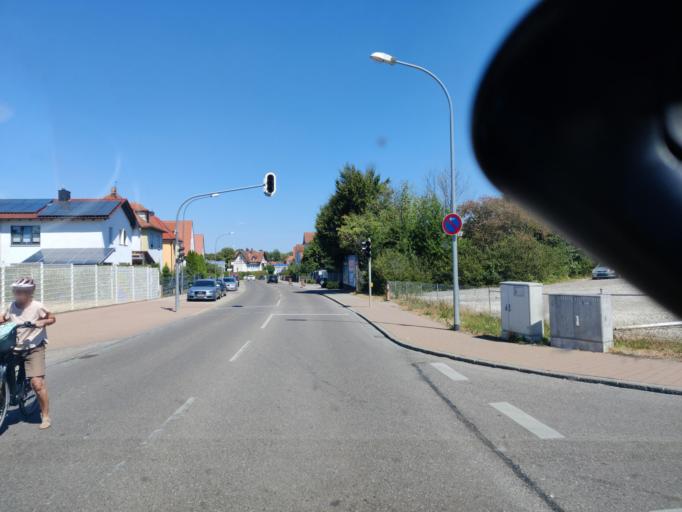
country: DE
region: Bavaria
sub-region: Regierungsbezirk Mittelfranken
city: Weissenburg in Bayern
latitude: 49.0224
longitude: 10.9664
